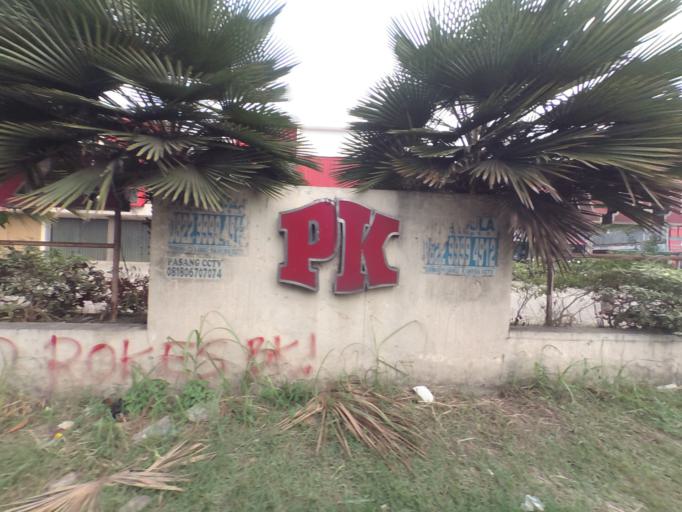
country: ID
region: West Java
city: Ciampea
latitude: -6.5589
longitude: 106.6918
